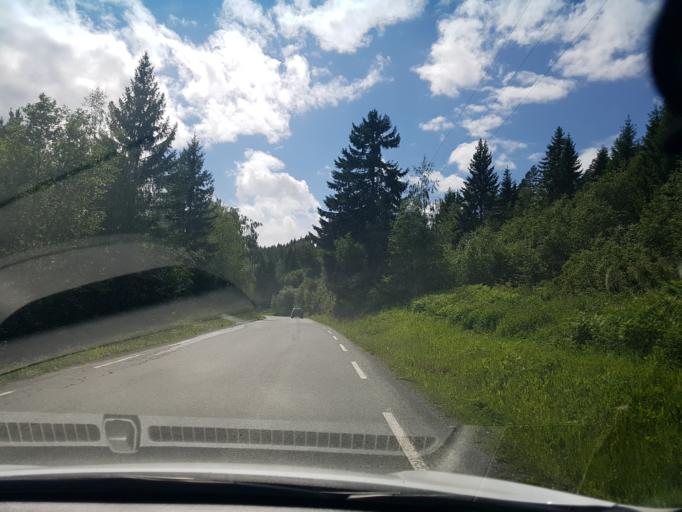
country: NO
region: Nord-Trondelag
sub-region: Frosta
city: Frosta
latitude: 63.6072
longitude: 10.8805
